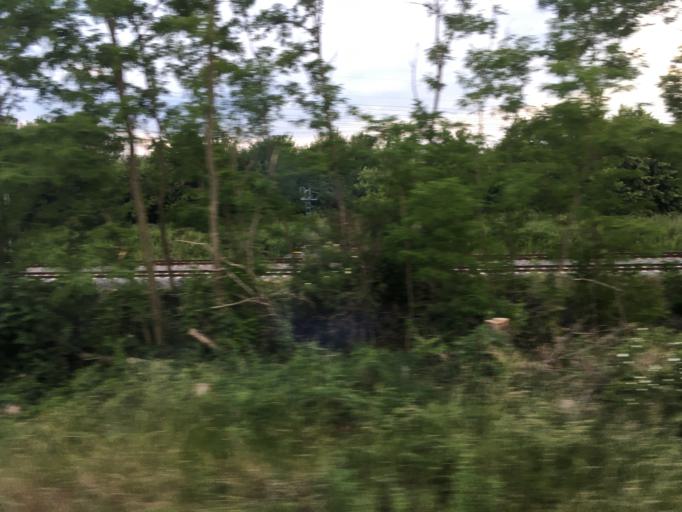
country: DE
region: Saxony
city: Taucha
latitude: 51.3710
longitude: 12.4352
